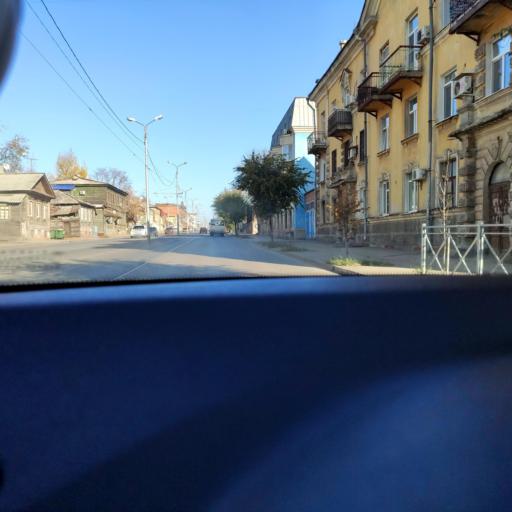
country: RU
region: Samara
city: Rozhdestveno
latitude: 53.1807
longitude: 50.0870
